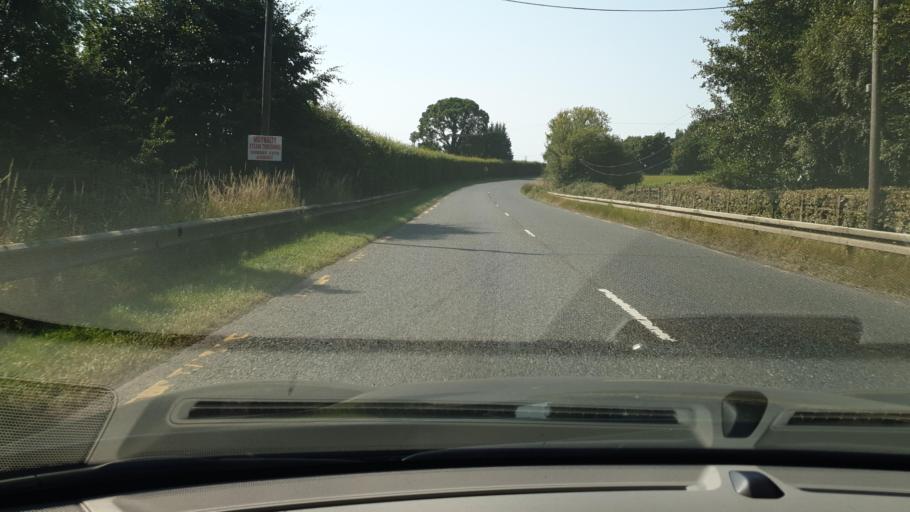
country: IE
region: Leinster
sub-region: An Mhi
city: Newtown Trim
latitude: 53.5156
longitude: -6.7631
